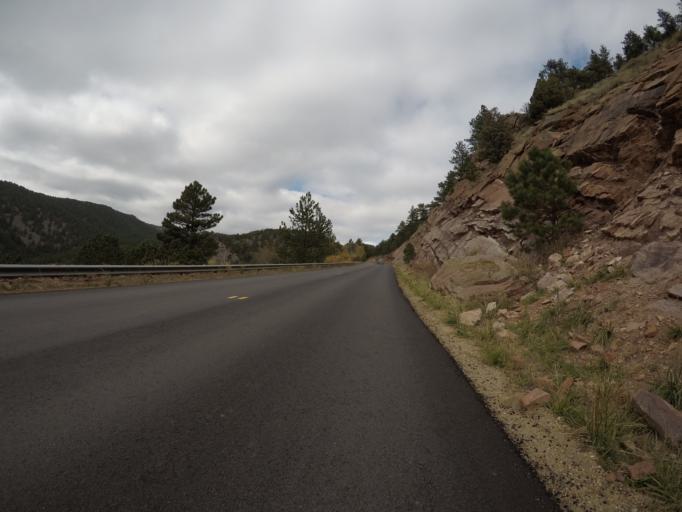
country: US
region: Colorado
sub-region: Boulder County
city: Boulder
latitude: 40.0678
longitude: -105.3076
